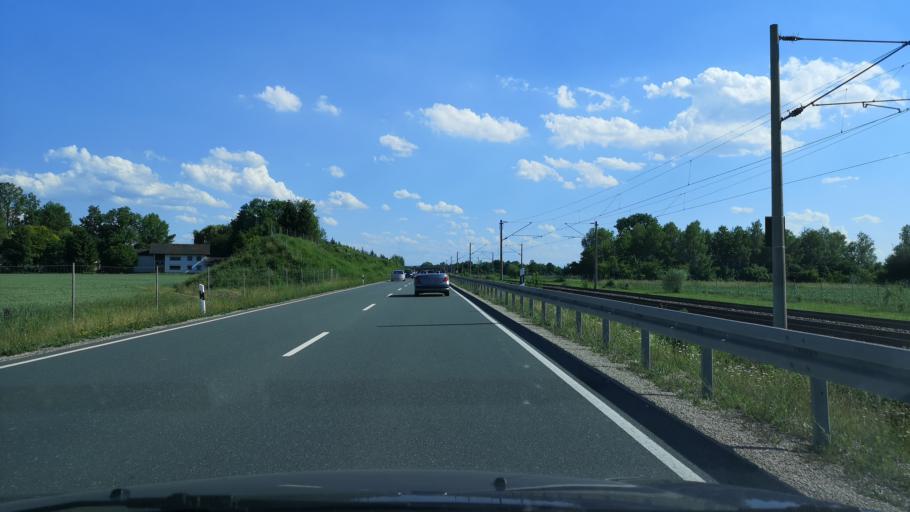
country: DE
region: Bavaria
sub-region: Upper Bavaria
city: Ismaning
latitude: 48.2735
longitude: 11.7104
